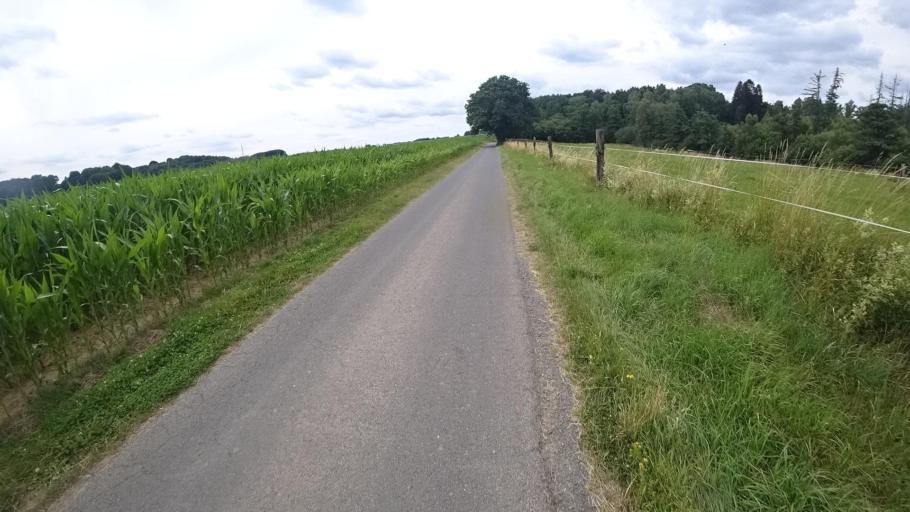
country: DE
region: Rheinland-Pfalz
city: Berzhausen
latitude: 50.6732
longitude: 7.5675
